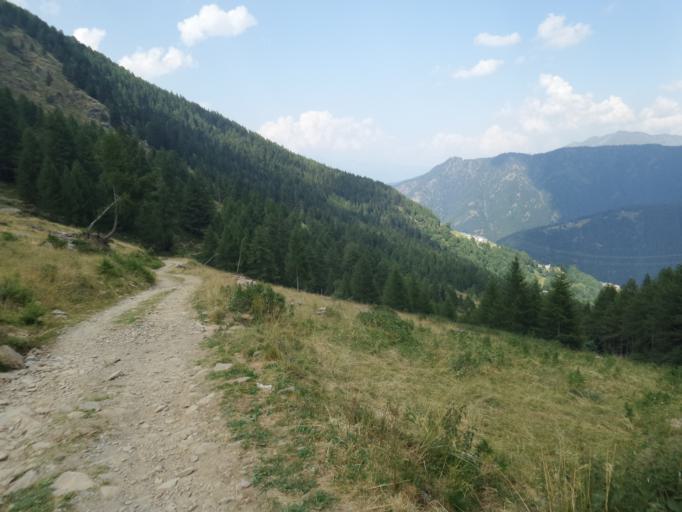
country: IT
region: Lombardy
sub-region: Provincia di Sondrio
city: Gerola Alta
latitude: 46.0586
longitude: 9.5225
